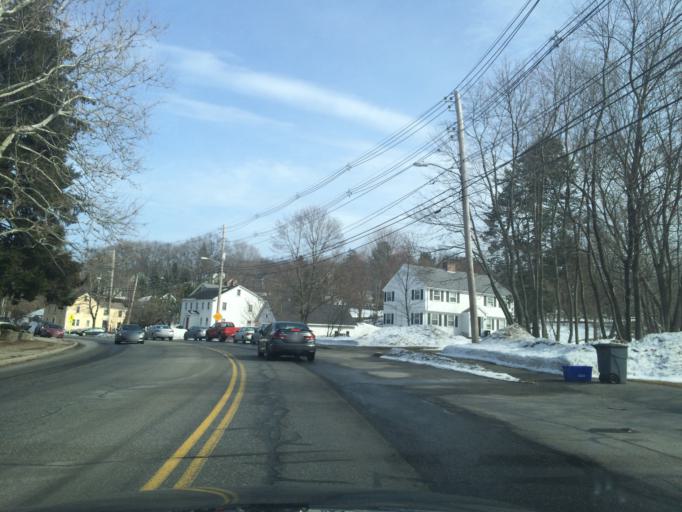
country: US
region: Massachusetts
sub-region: Middlesex County
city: Lexington
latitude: 42.4275
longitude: -71.2049
